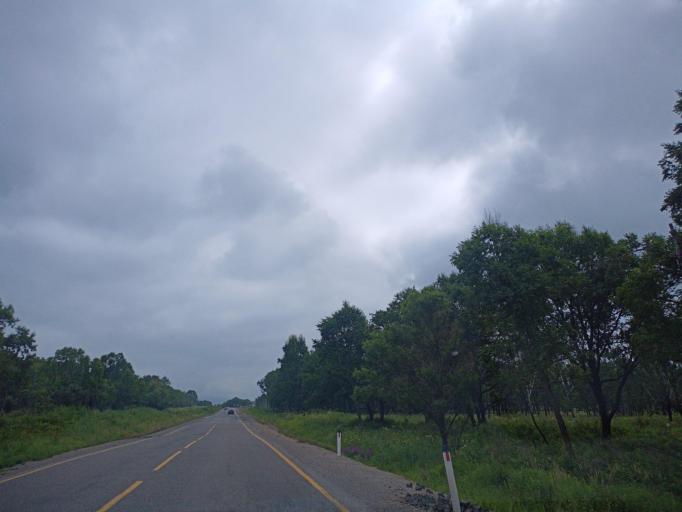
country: RU
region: Primorskiy
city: Dal'nerechensk
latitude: 46.0398
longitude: 133.8913
